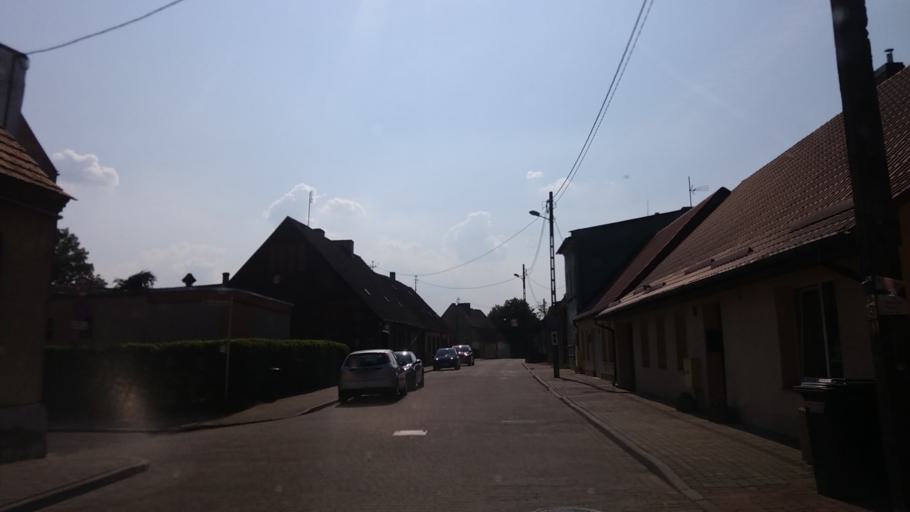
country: PL
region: West Pomeranian Voivodeship
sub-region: Powiat choszczenski
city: Drawno
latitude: 53.2203
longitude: 15.7573
